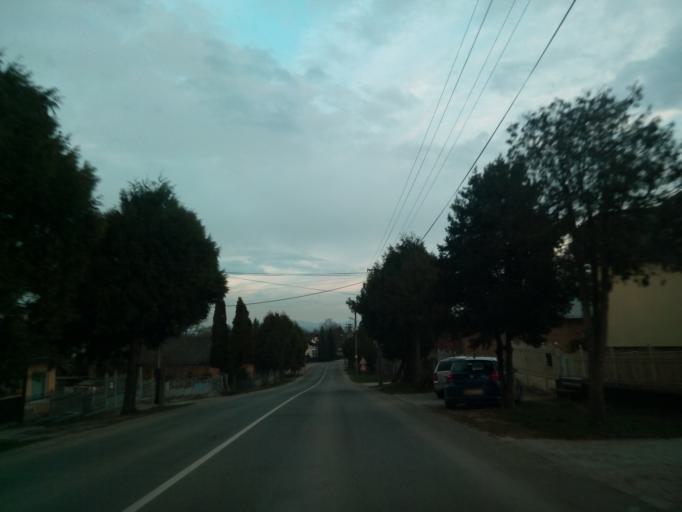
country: SK
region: Kosicky
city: Moldava nad Bodvou
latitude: 48.5992
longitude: 21.0147
